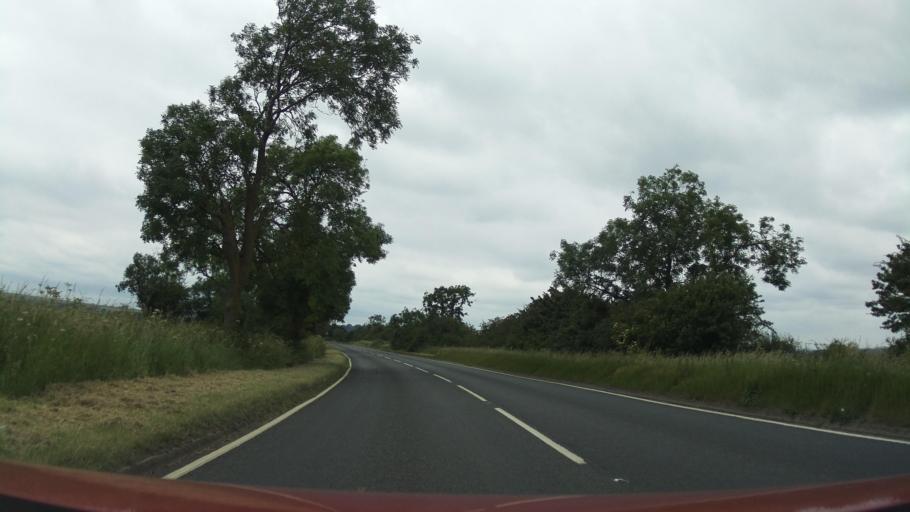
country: GB
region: England
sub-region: Leicestershire
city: Melton Mowbray
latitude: 52.7245
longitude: -0.8373
